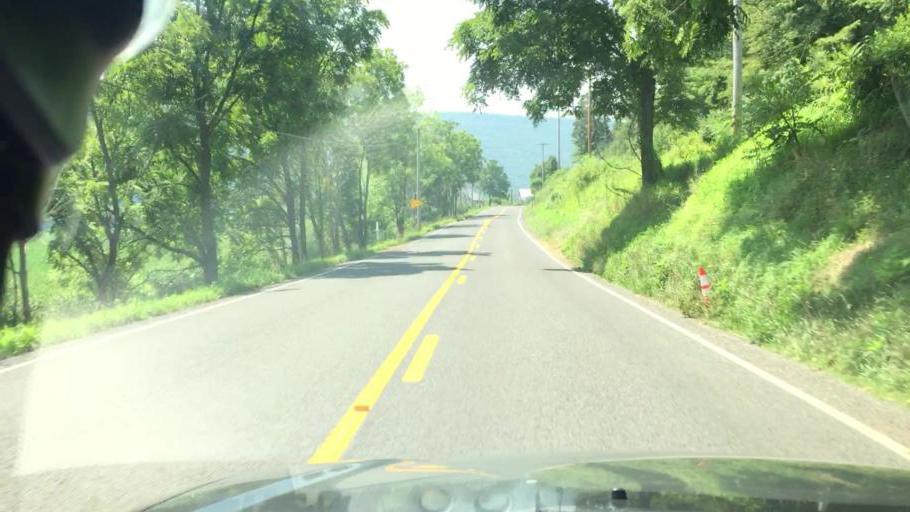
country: US
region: Pennsylvania
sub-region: Columbia County
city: Mifflinville
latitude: 41.0097
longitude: -76.3190
